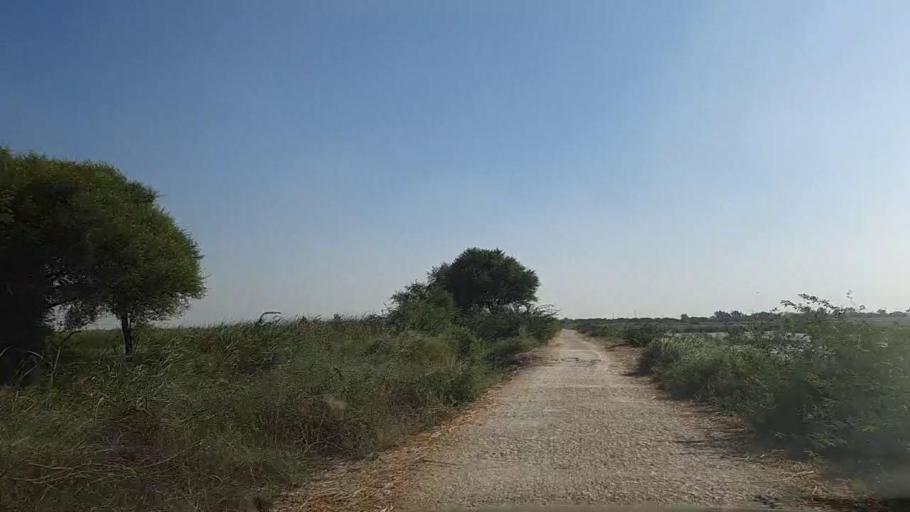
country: PK
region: Sindh
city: Daro Mehar
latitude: 24.7535
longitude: 68.0628
